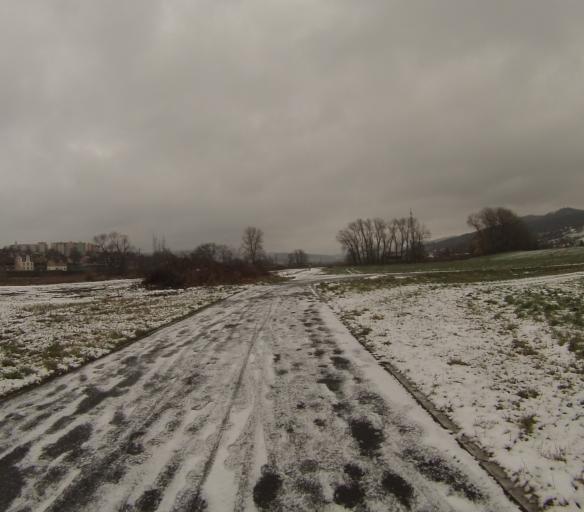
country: CZ
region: Ustecky
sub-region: Okres Decin
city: Decin
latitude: 50.7521
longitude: 14.1886
